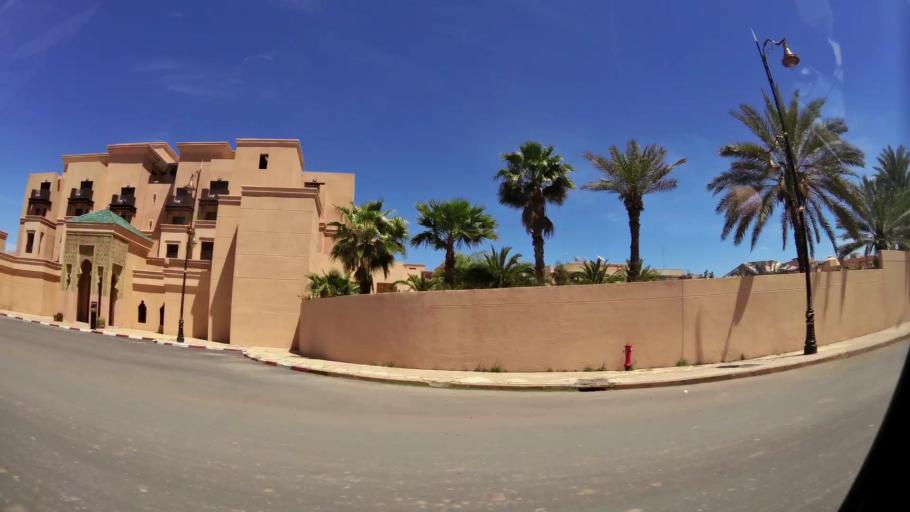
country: MA
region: Marrakech-Tensift-Al Haouz
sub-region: Marrakech
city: Marrakesh
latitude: 31.6244
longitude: -8.0164
